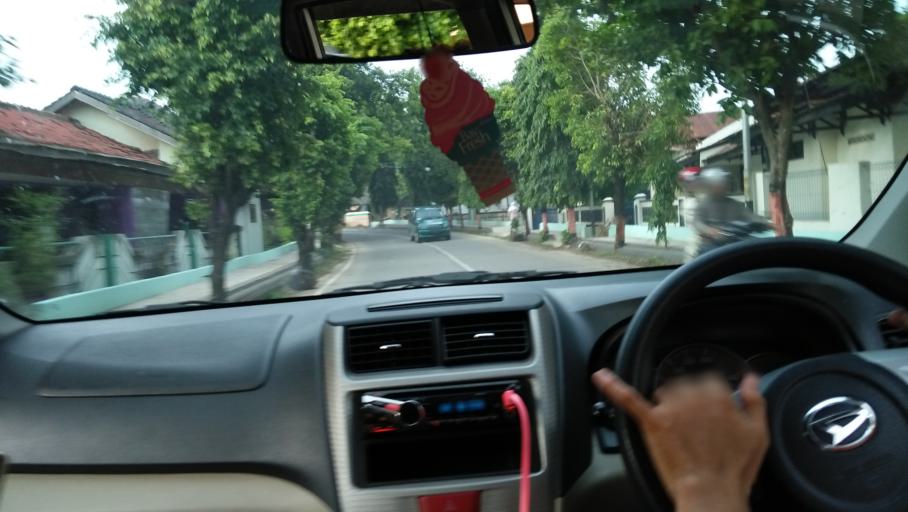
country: ID
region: Central Java
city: Mlonggo
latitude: -6.5956
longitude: 110.6764
